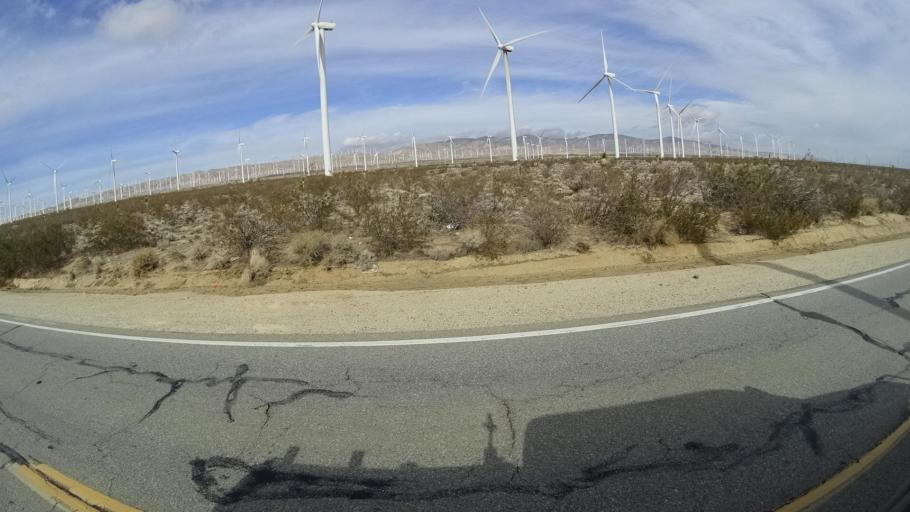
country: US
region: California
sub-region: Kern County
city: Mojave
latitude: 35.0442
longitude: -118.2254
